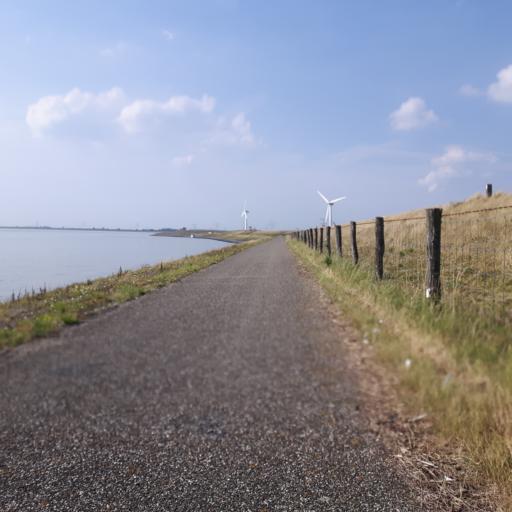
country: NL
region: Zeeland
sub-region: Gemeente Reimerswaal
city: Yerseke
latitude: 51.4510
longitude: 3.9941
